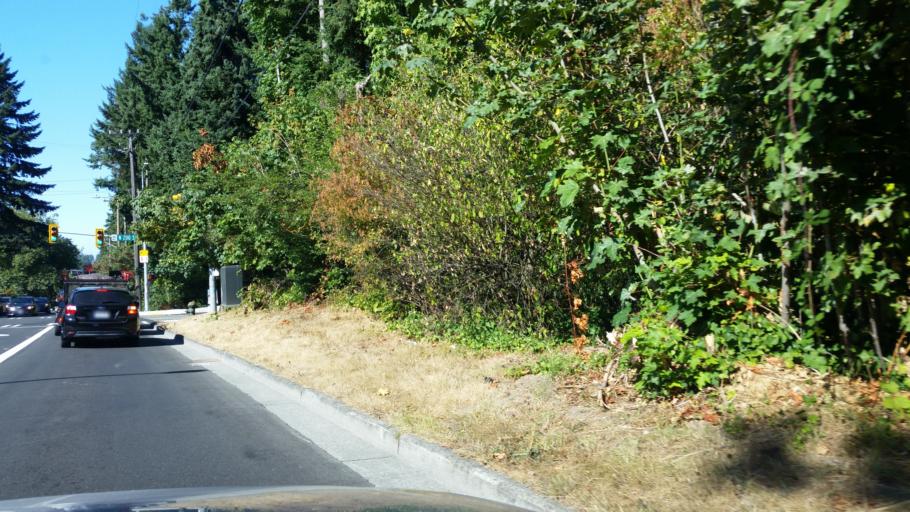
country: US
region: Washington
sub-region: King County
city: Shoreline
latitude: 47.7738
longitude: -122.3352
